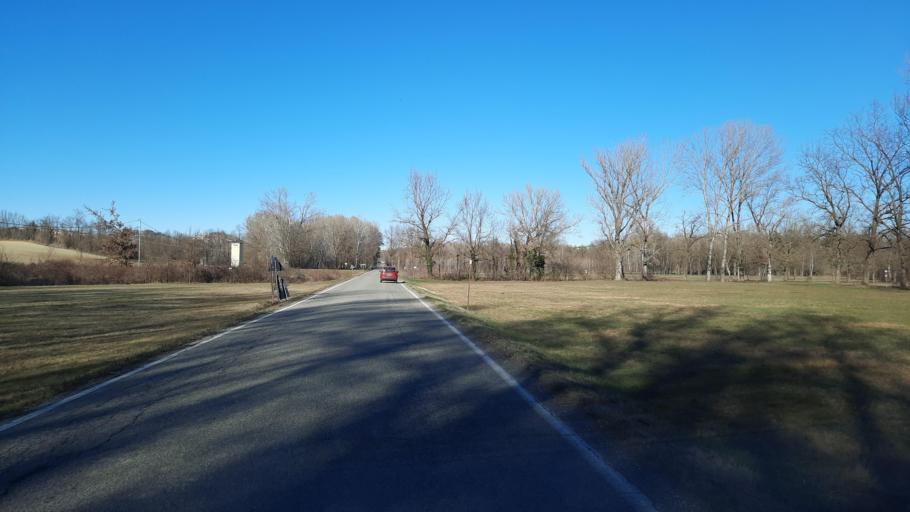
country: IT
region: Piedmont
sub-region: Provincia di Alessandria
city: Frassinello Monferrato
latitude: 45.0490
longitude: 8.3934
